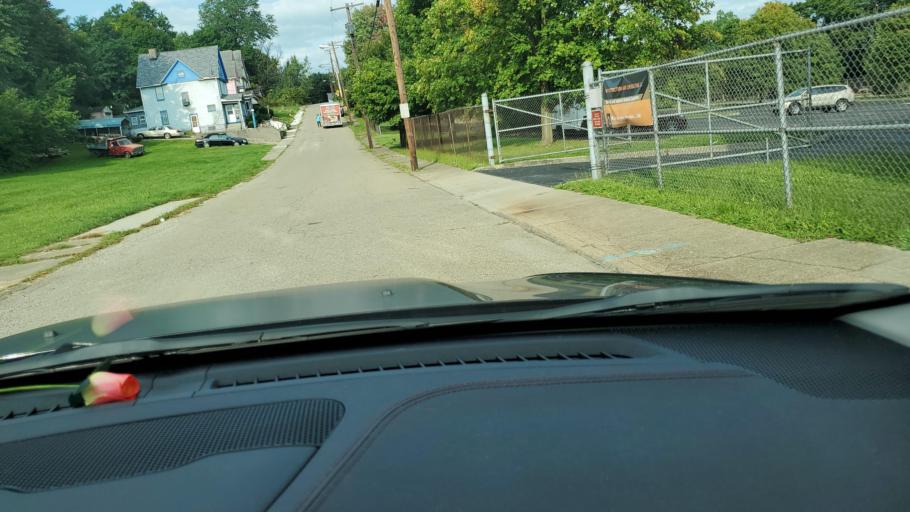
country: US
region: Ohio
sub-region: Mahoning County
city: Youngstown
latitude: 41.0953
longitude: -80.6598
